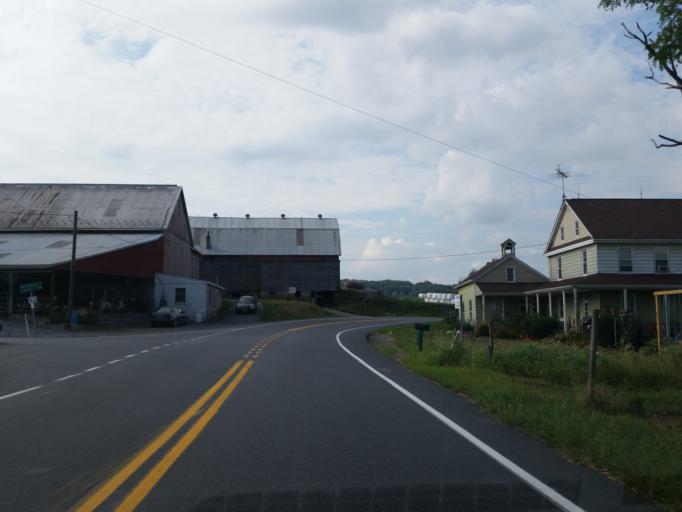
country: US
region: Pennsylvania
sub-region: Lancaster County
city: Mount Joy
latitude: 40.2115
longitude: -76.5066
